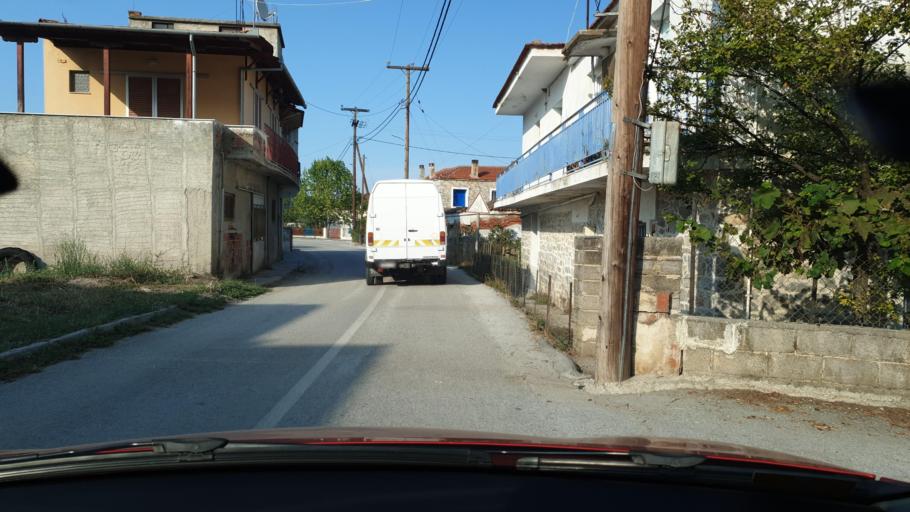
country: GR
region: Thessaly
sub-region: Nomos Magnisias
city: Pteleos
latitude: 39.0045
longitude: 22.9633
